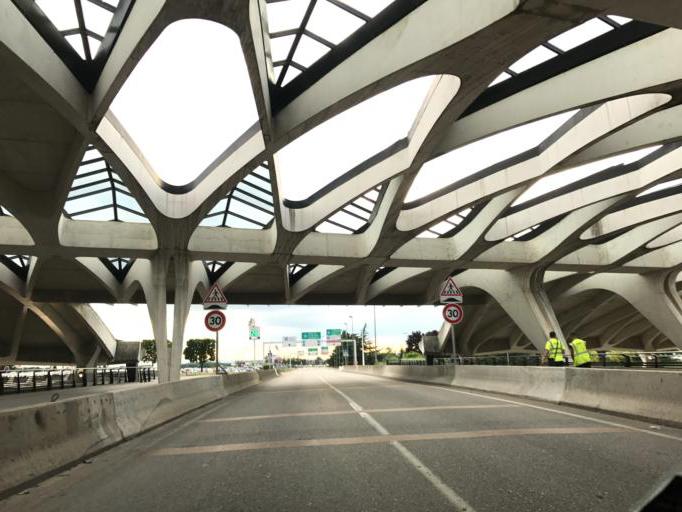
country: FR
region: Rhone-Alpes
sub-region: Departement du Rhone
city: Pusignan
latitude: 45.7223
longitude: 5.0762
